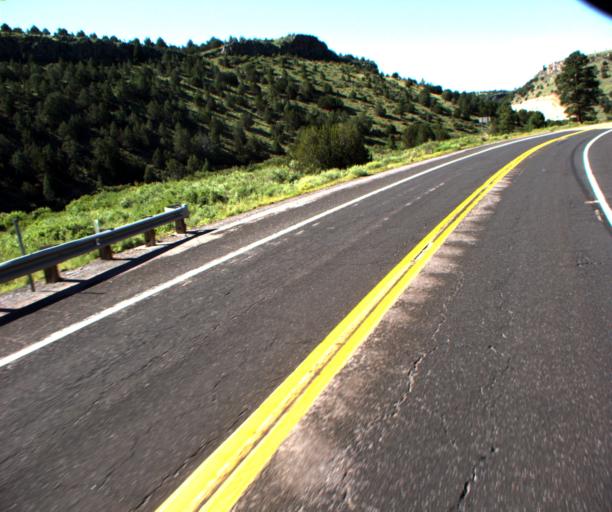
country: US
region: Arizona
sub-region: Apache County
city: Eagar
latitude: 34.0769
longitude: -109.1984
